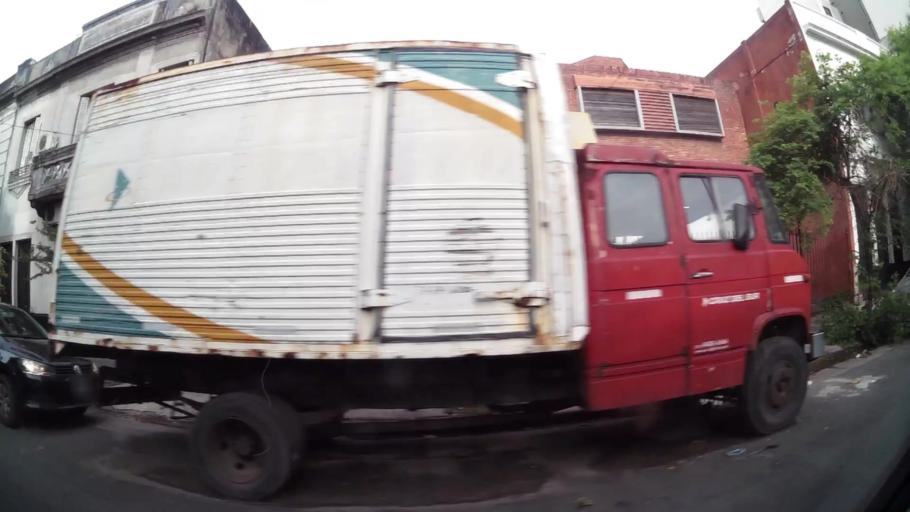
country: AR
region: Buenos Aires F.D.
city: Buenos Aires
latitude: -34.6266
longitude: -58.4186
